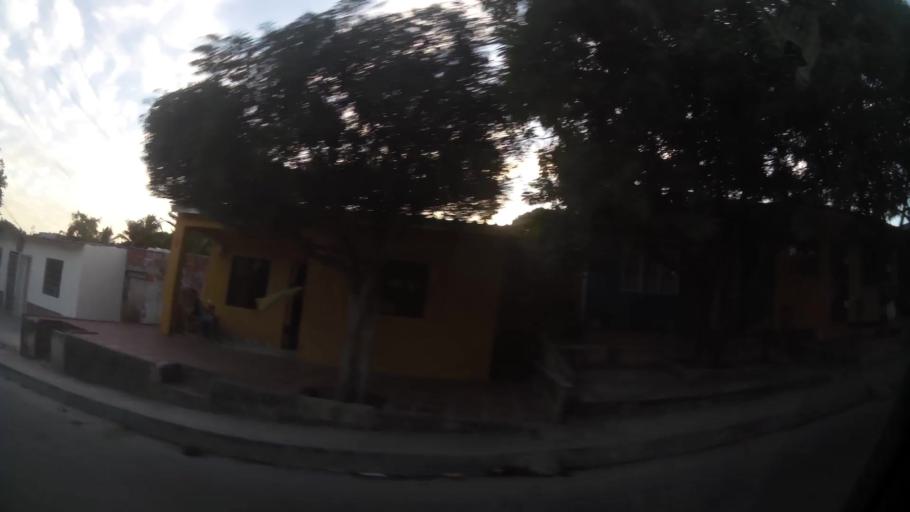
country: CO
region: Atlantico
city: Barranquilla
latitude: 10.9626
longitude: -74.8279
